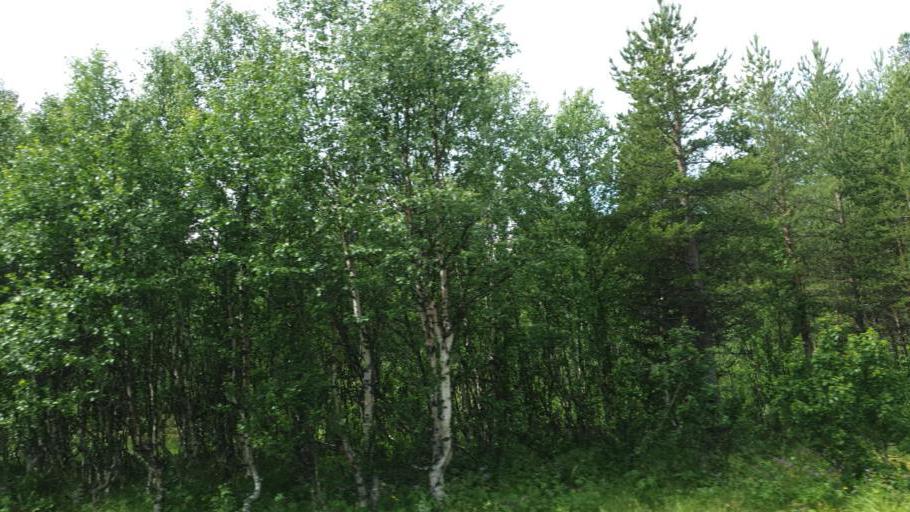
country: NO
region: Oppland
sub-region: Vaga
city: Vagamo
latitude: 61.6993
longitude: 9.0594
